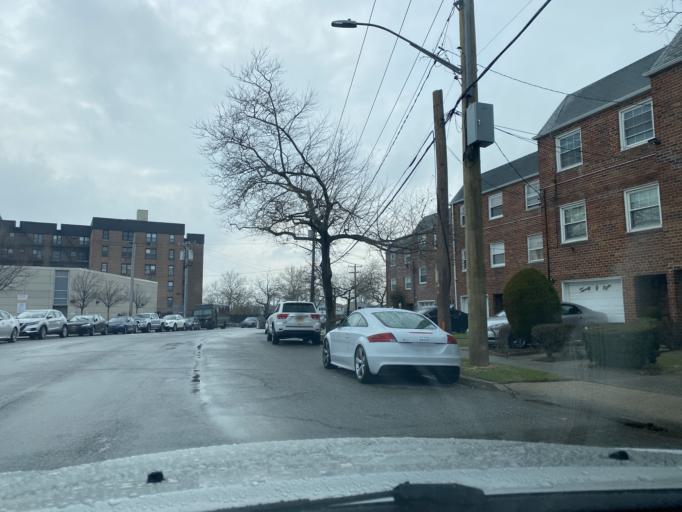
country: US
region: New York
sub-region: Nassau County
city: Inwood
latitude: 40.5974
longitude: -73.7545
